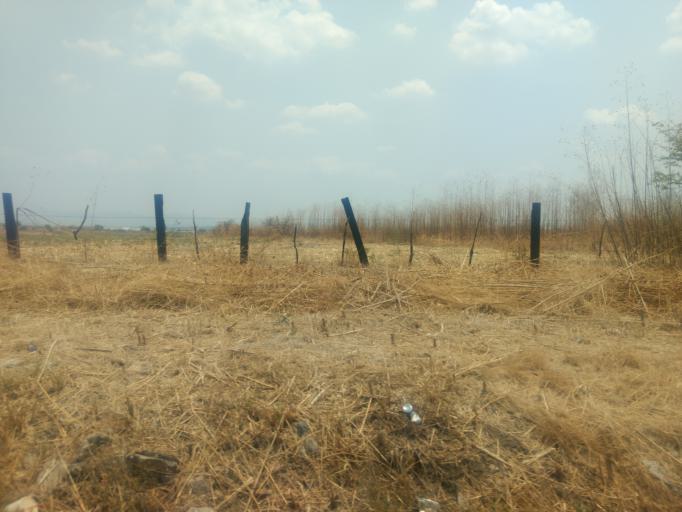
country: MX
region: Morelos
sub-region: Mazatepec
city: Cuauchichinola
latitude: 18.6398
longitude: -99.3856
